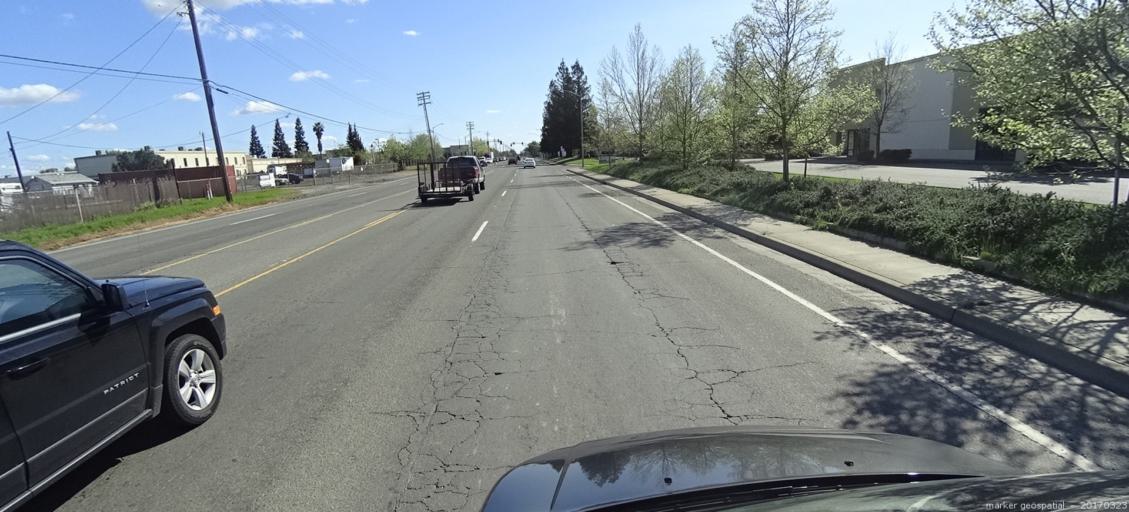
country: US
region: California
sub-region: Sacramento County
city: Florin
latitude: 38.5080
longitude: -121.3907
